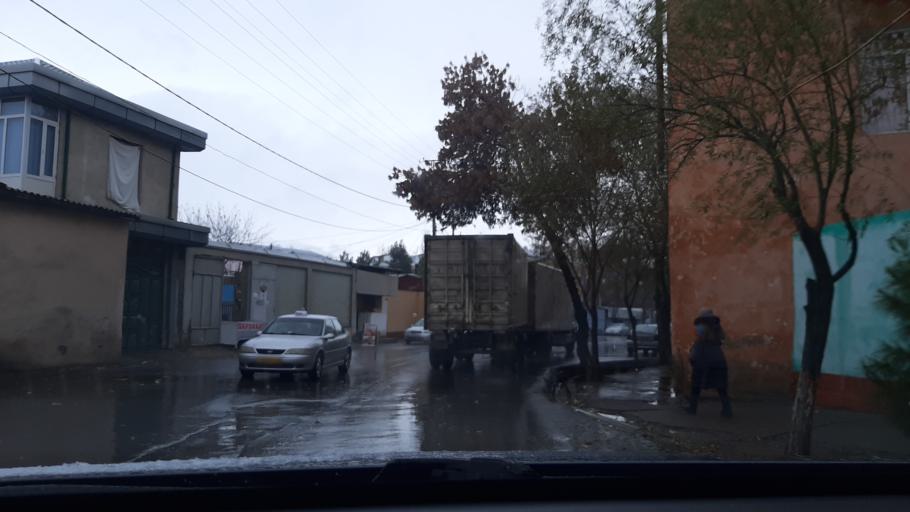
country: TJ
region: Viloyati Sughd
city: Khujand
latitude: 40.2725
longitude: 69.6385
